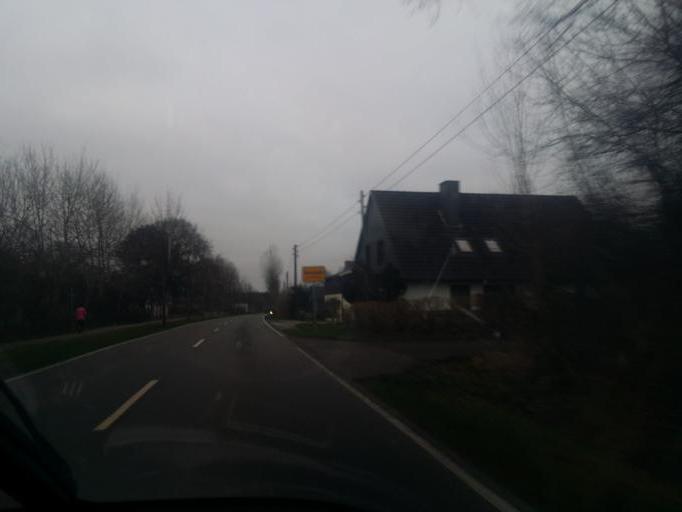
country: DE
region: Schleswig-Holstein
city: Fedderingen
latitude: 54.2893
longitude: 9.1467
